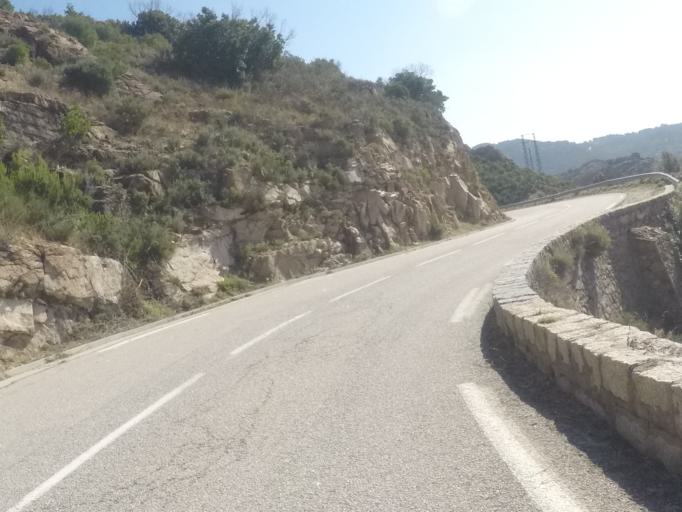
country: FR
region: Corsica
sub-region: Departement de la Corse-du-Sud
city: Zonza
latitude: 41.7674
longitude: 9.0471
